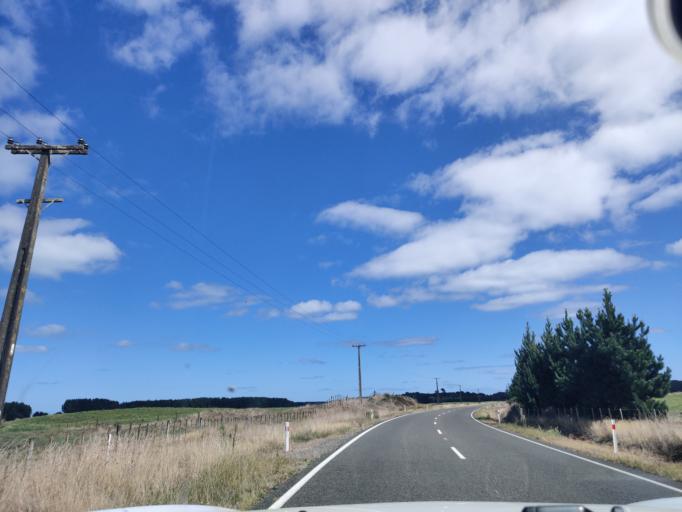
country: NZ
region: Manawatu-Wanganui
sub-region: Horowhenua District
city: Foxton
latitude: -40.3826
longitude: 175.2690
